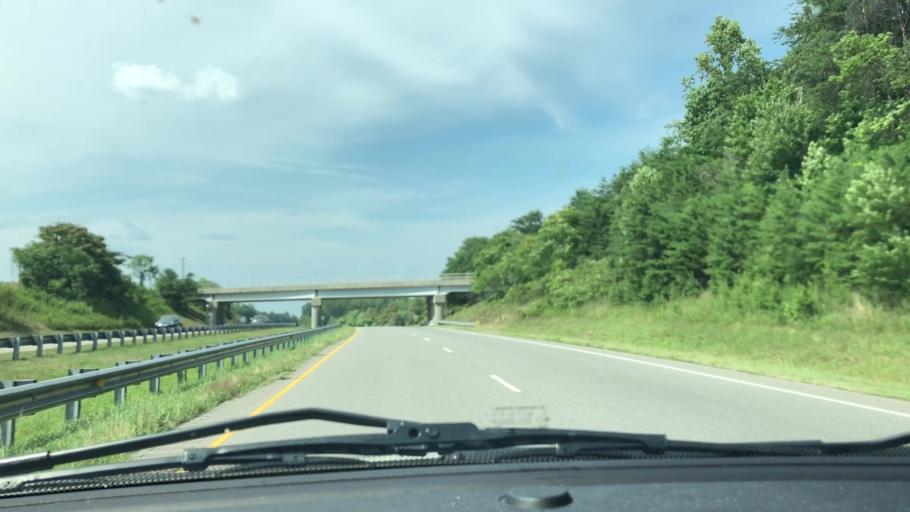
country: US
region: North Carolina
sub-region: Rockingham County
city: Stoneville
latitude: 36.5312
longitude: -79.9142
